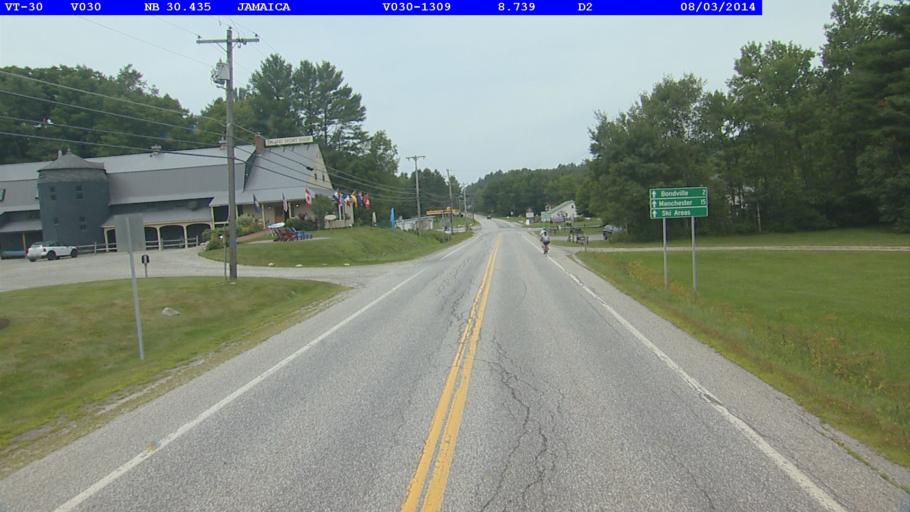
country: US
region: Vermont
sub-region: Windham County
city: Dover
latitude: 43.1462
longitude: -72.8395
